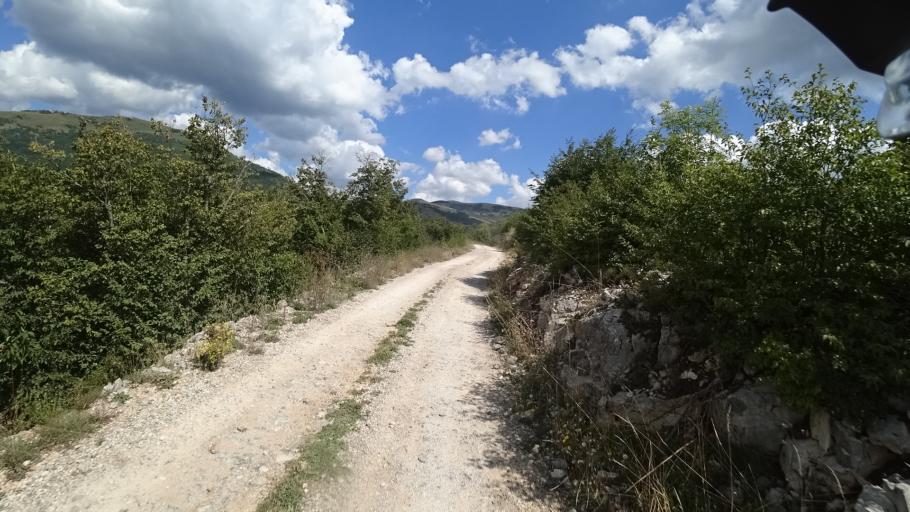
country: HR
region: Zadarska
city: Gracac
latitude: 44.5467
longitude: 15.8150
